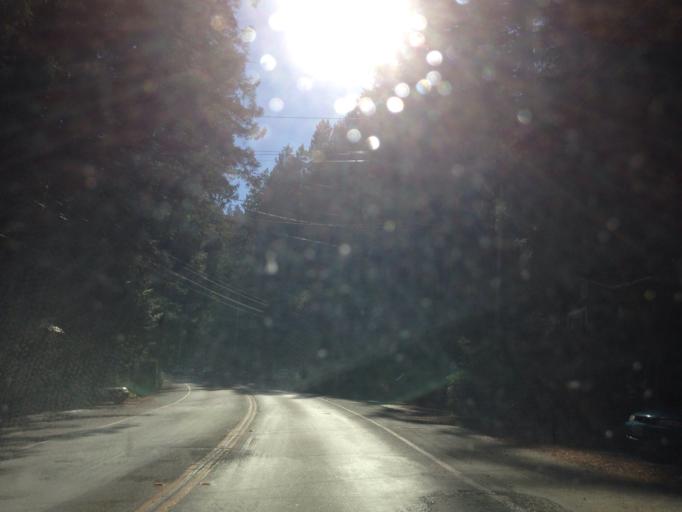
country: US
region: California
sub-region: Sonoma County
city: Guerneville
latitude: 38.4928
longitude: -123.0142
